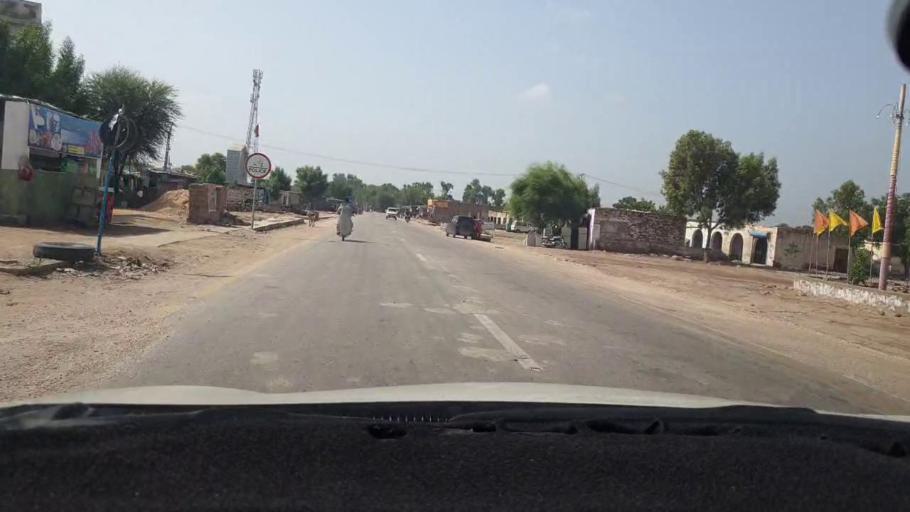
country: PK
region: Sindh
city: Mirpur Khas
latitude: 25.6650
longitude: 69.1026
